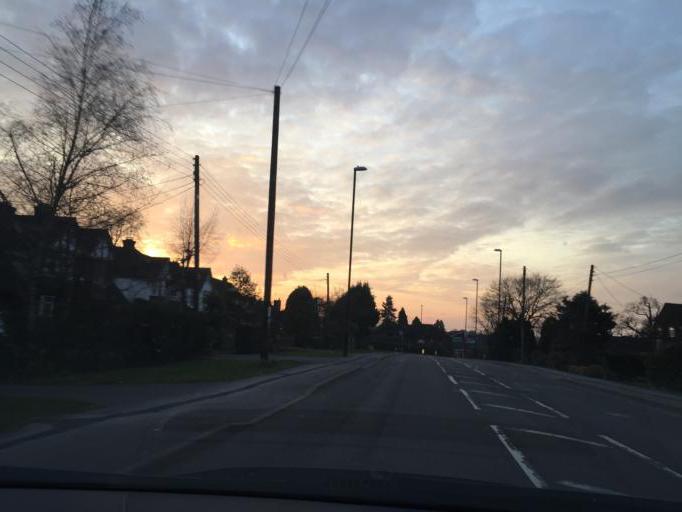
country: GB
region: England
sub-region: Warwickshire
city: Kenilworth
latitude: 52.3889
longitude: -1.5971
